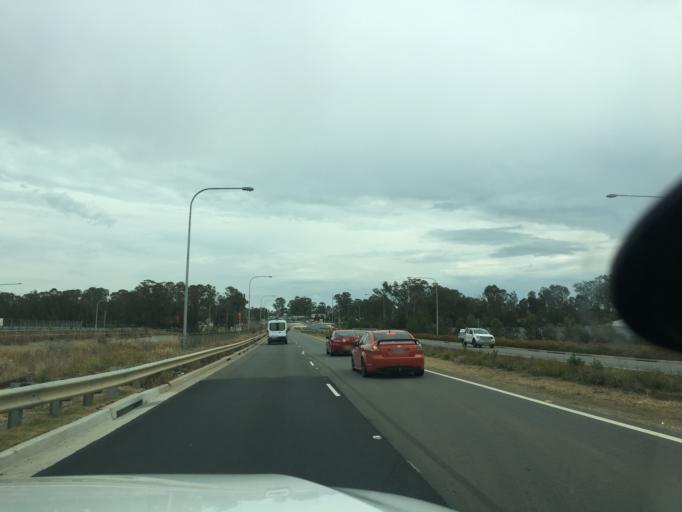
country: AU
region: New South Wales
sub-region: Campbelltown Municipality
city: Denham Court
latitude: -33.9603
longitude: 150.8227
